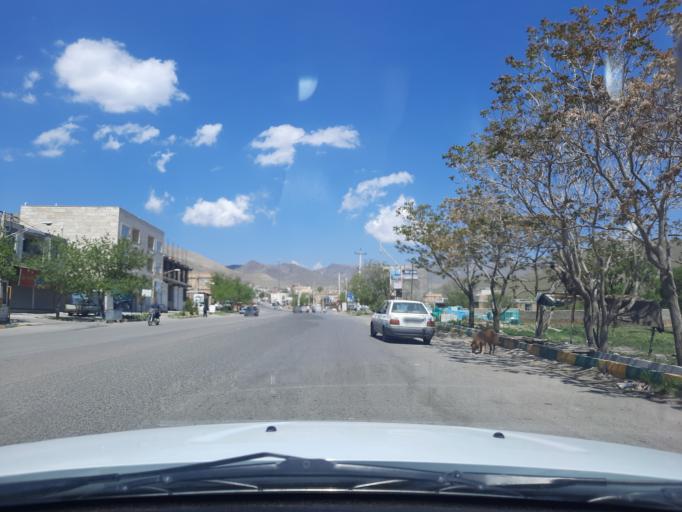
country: IR
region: Qazvin
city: Qazvin
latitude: 36.3299
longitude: 50.1493
